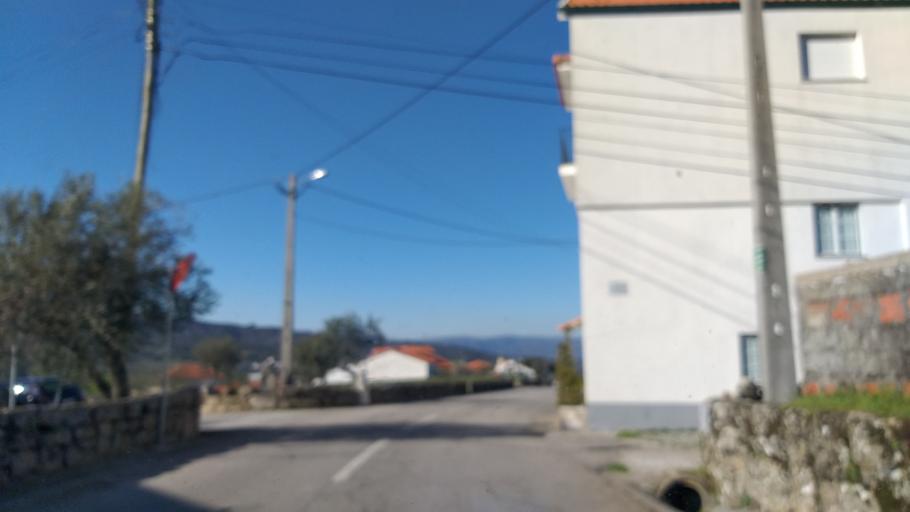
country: PT
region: Guarda
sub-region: Celorico da Beira
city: Celorico da Beira
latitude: 40.5841
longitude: -7.3600
